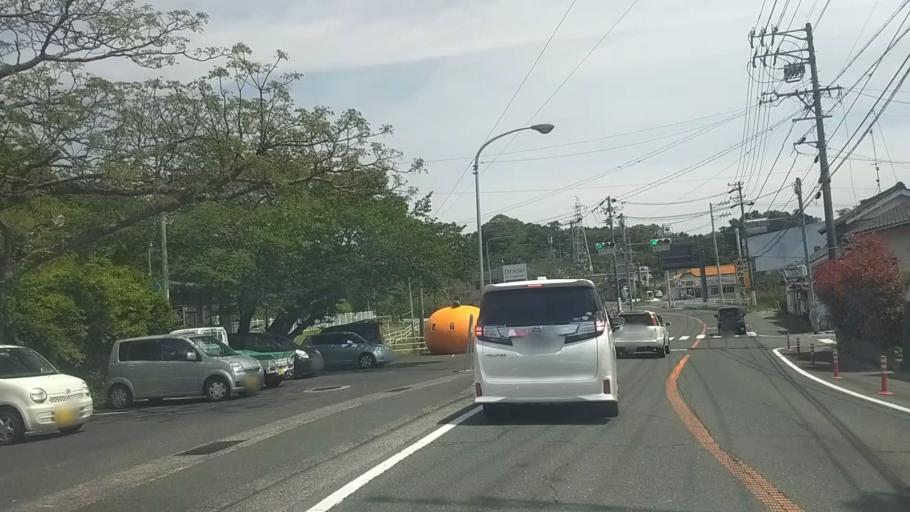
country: JP
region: Shizuoka
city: Kosai-shi
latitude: 34.7904
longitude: 137.5862
